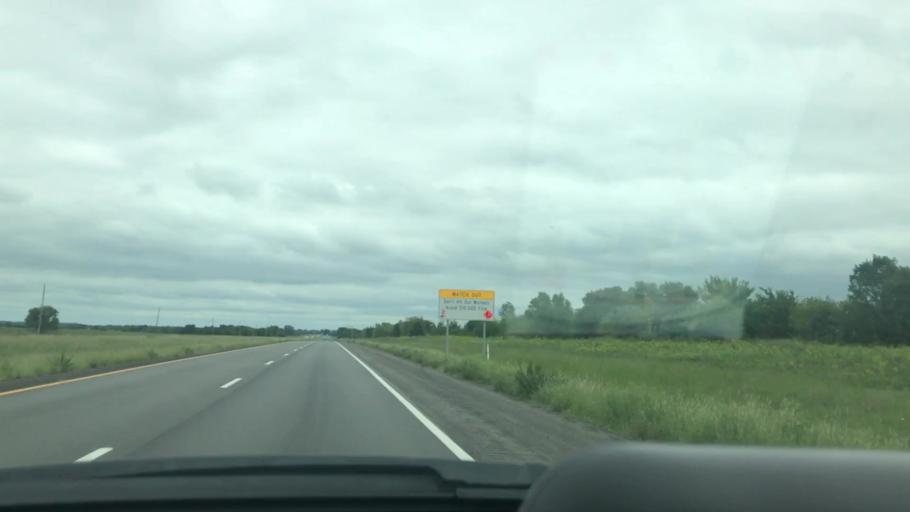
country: US
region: Oklahoma
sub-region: Mayes County
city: Pryor
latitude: 36.4539
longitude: -95.2646
